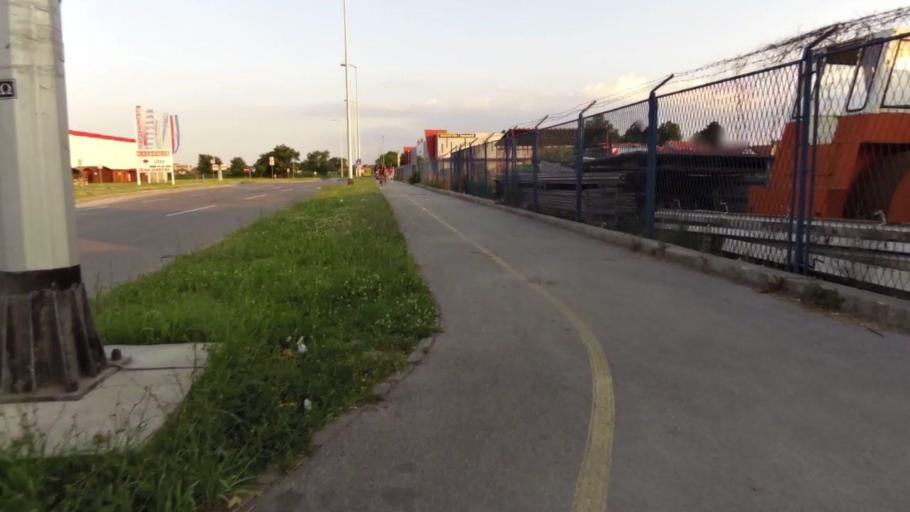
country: HR
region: Grad Zagreb
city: Dubrava
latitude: 45.7974
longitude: 16.0500
